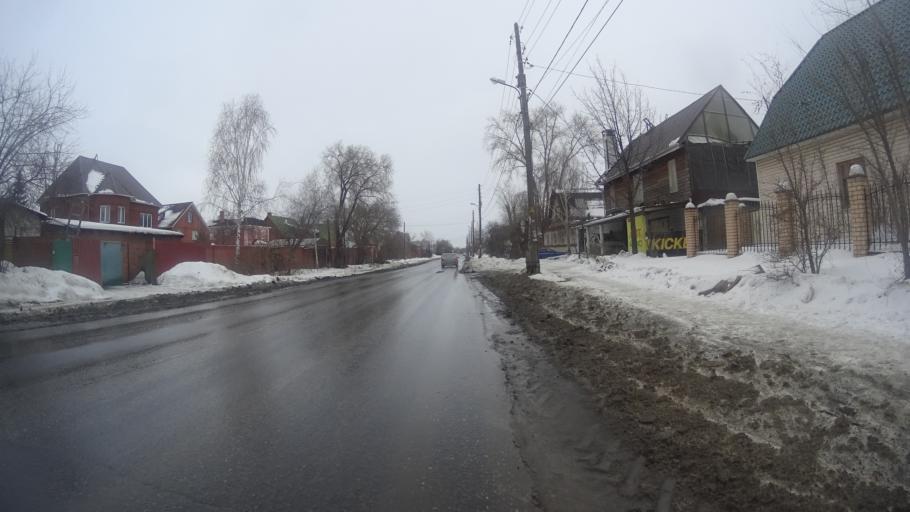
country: RU
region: Chelyabinsk
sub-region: Gorod Chelyabinsk
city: Chelyabinsk
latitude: 55.1339
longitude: 61.3805
